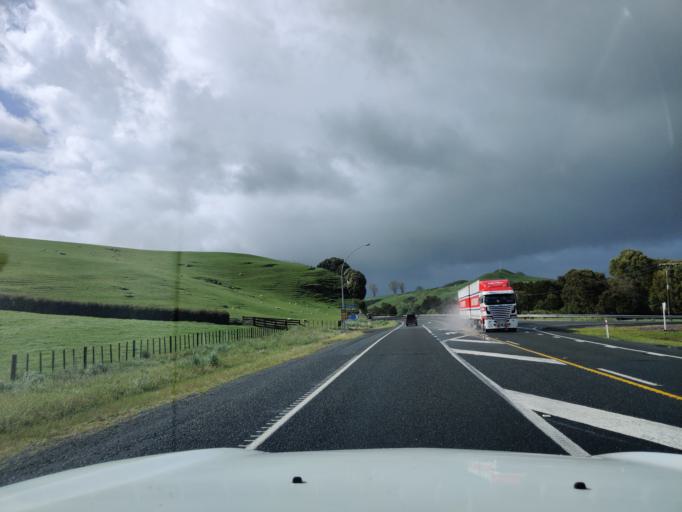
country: NZ
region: Waikato
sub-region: Matamata-Piako District
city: Matamata
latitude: -37.9498
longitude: 175.6743
